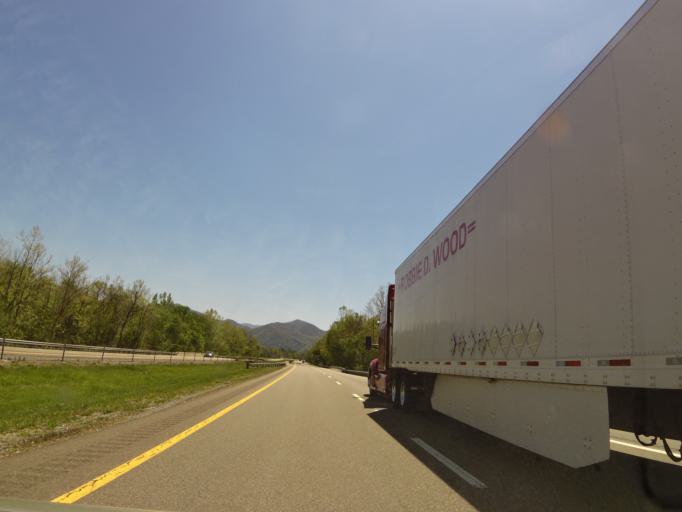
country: US
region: Tennessee
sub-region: Unicoi County
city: Erwin
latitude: 36.1441
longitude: -82.4276
